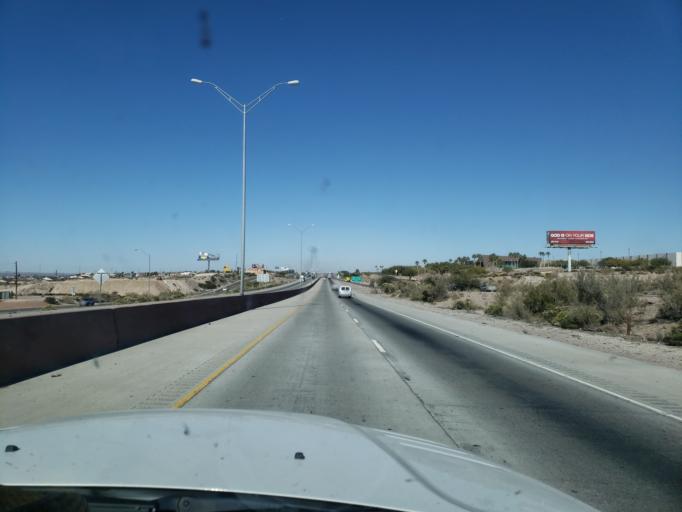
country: US
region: Texas
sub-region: El Paso County
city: Canutillo
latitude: 31.8689
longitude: -106.5784
